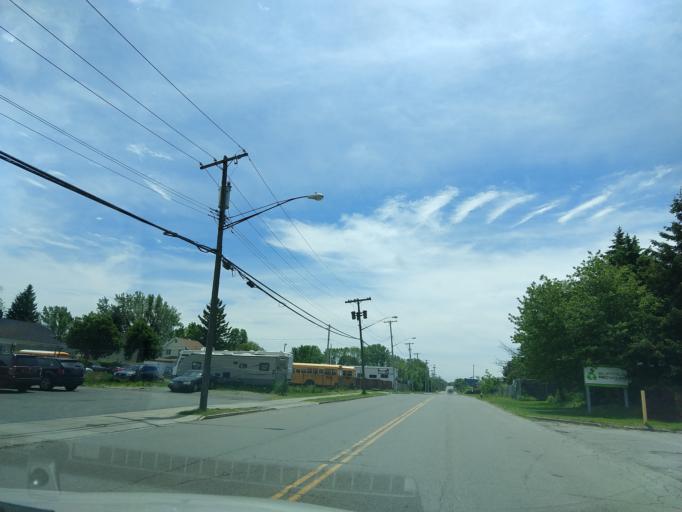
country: US
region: New York
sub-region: Erie County
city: Lackawanna
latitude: 42.8458
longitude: -78.8323
